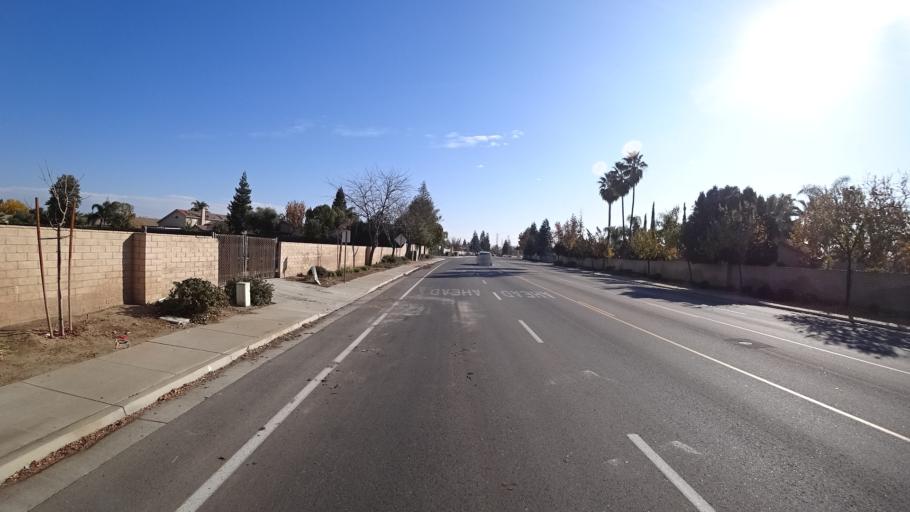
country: US
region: California
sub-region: Kern County
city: Greenacres
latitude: 35.3913
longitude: -119.1021
